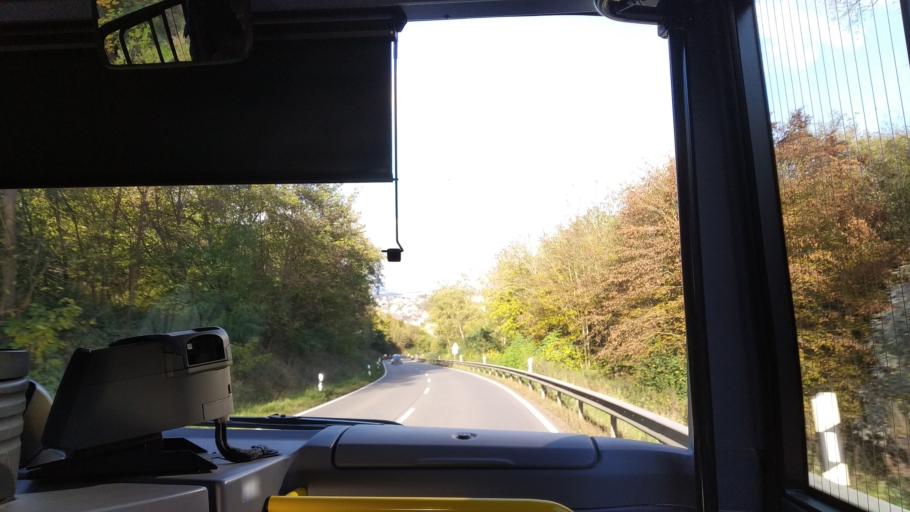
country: DE
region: Rheinland-Pfalz
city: Diez
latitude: 50.3627
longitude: 8.0227
